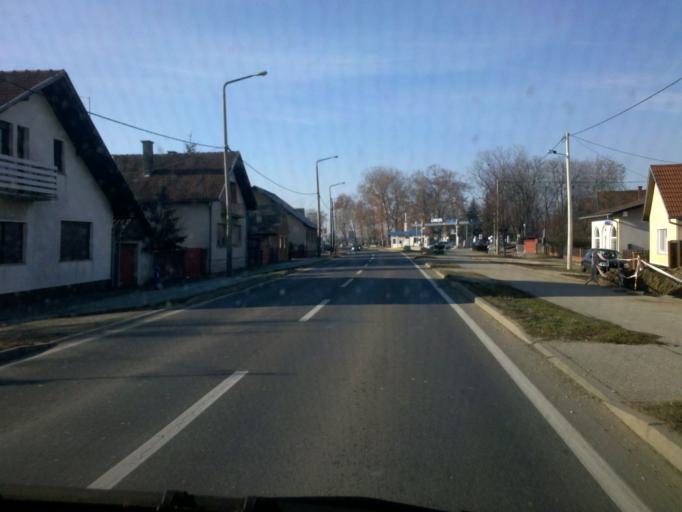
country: HR
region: Koprivnicko-Krizevacka
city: Kalinovac
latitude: 46.0297
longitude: 17.0686
